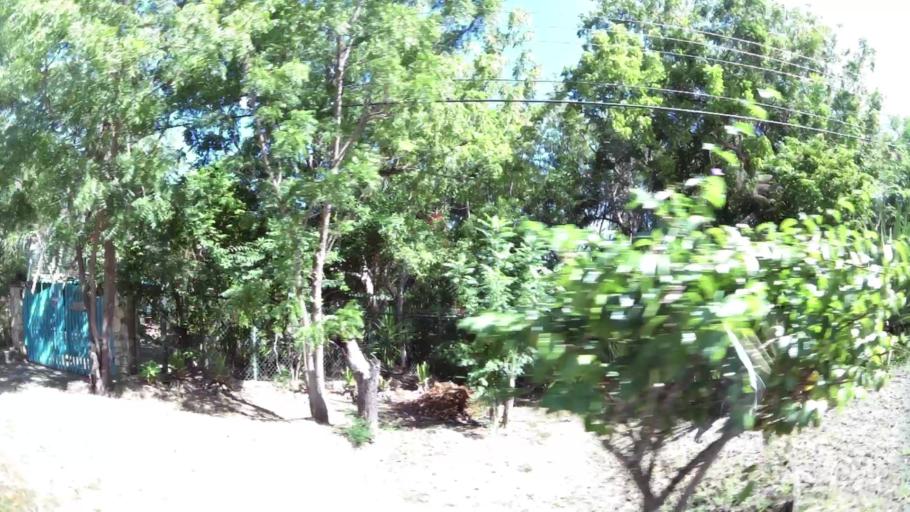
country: AG
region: Saint Paul
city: Falmouth
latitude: 17.0283
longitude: -61.7410
